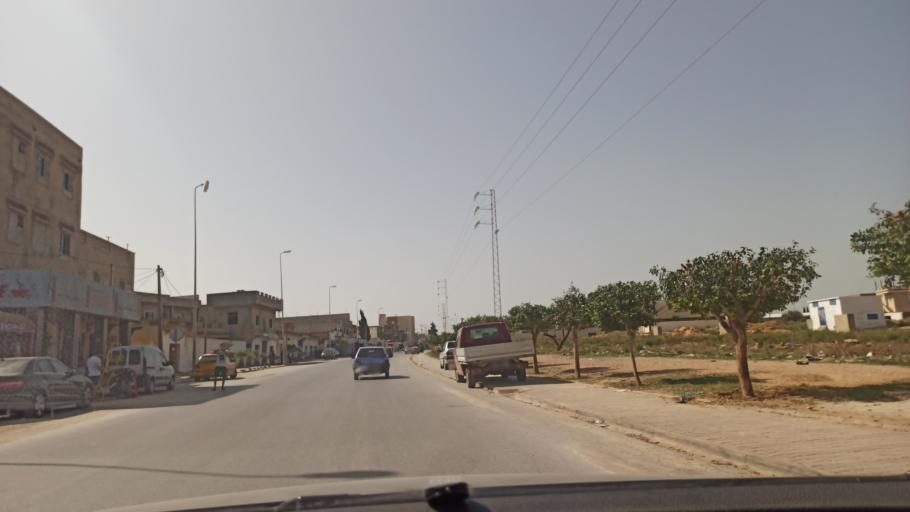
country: TN
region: Manouba
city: Manouba
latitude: 36.7635
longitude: 10.1096
